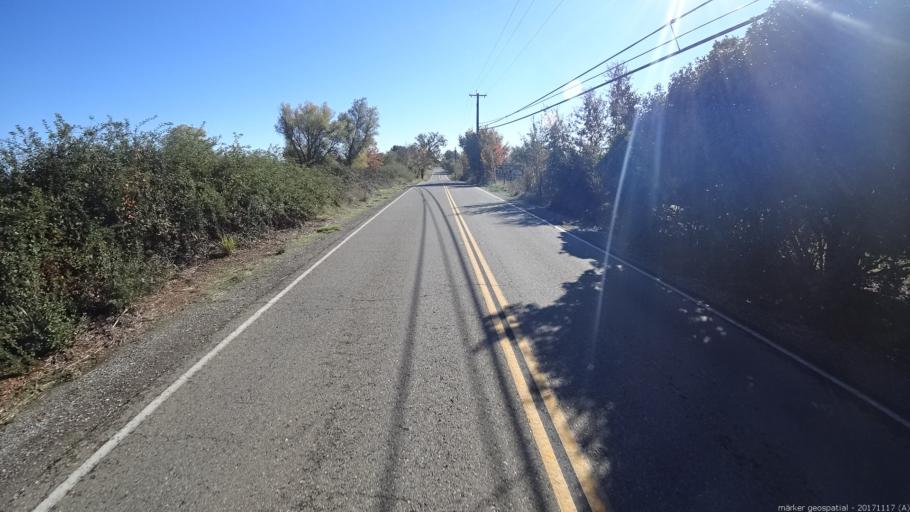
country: US
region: California
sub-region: Shasta County
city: Cottonwood
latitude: 40.4306
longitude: -122.2315
